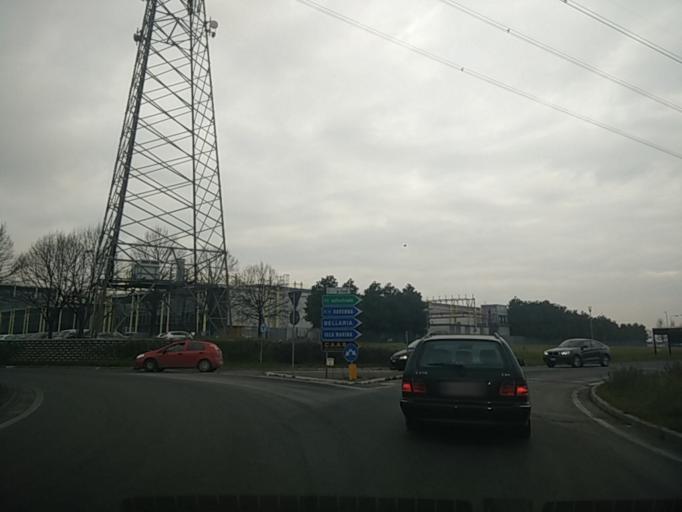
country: IT
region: Emilia-Romagna
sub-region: Provincia di Rimini
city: Santarcangelo
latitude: 44.0663
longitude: 12.4640
